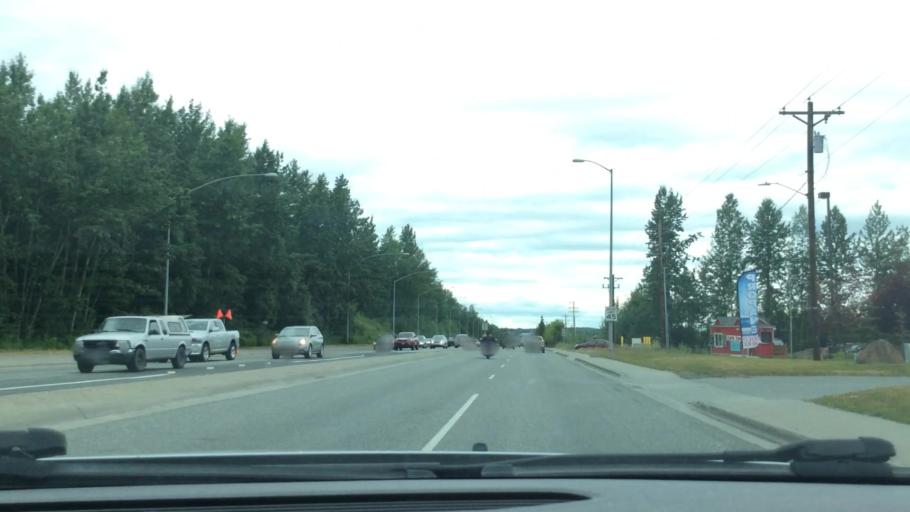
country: US
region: Alaska
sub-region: Anchorage Municipality
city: Anchorage
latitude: 61.2099
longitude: -149.7783
